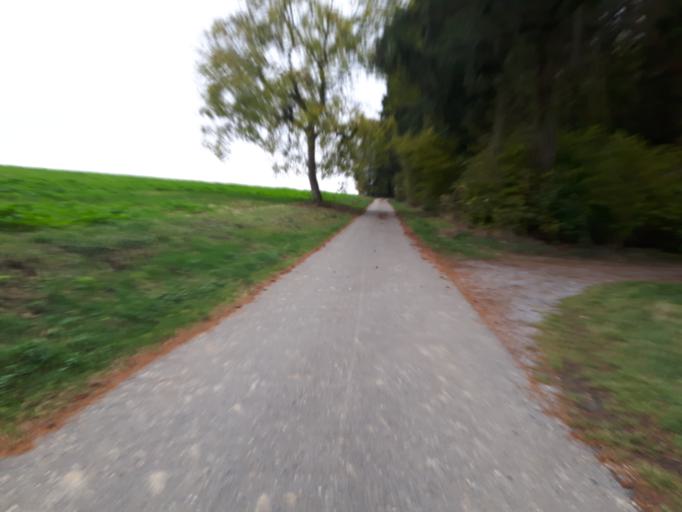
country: DE
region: Baden-Wuerttemberg
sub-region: Karlsruhe Region
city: Ostringen
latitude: 49.2002
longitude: 8.7300
